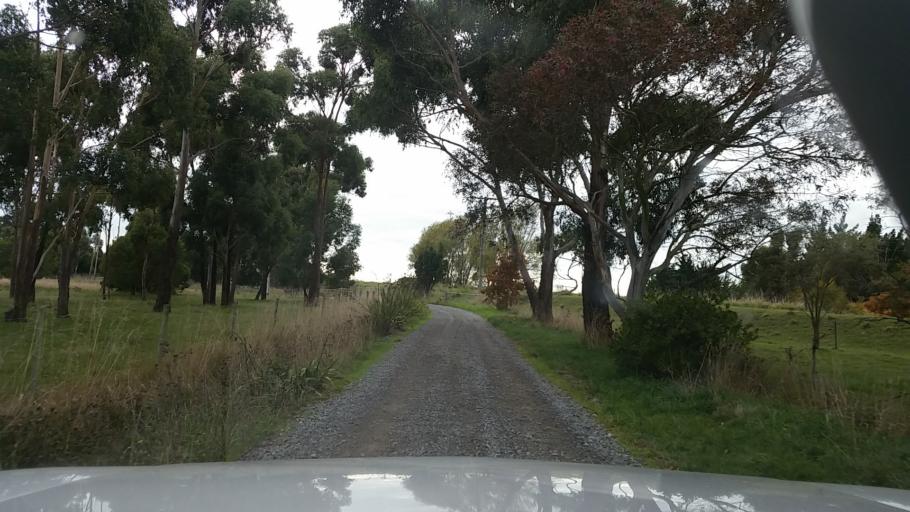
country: NZ
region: Marlborough
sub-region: Marlborough District
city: Blenheim
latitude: -41.5195
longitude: 174.0403
